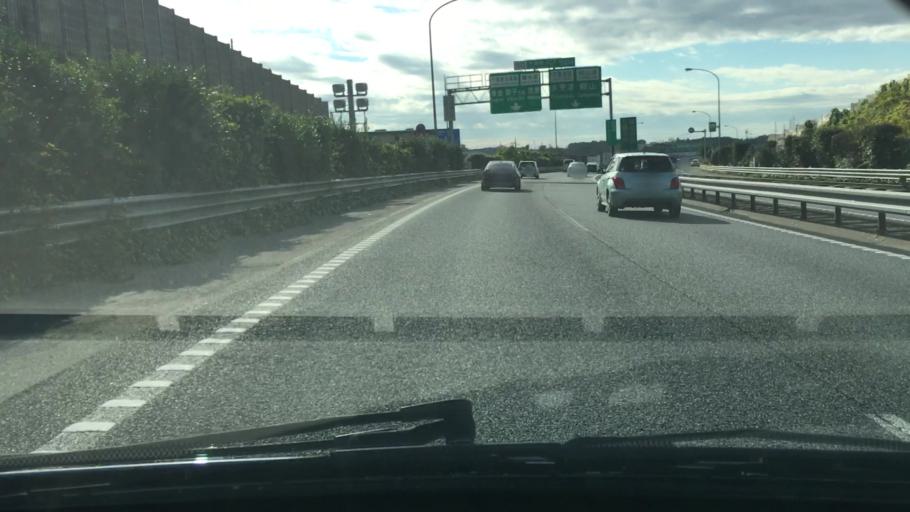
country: JP
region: Chiba
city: Chiba
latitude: 35.6121
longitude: 140.1532
